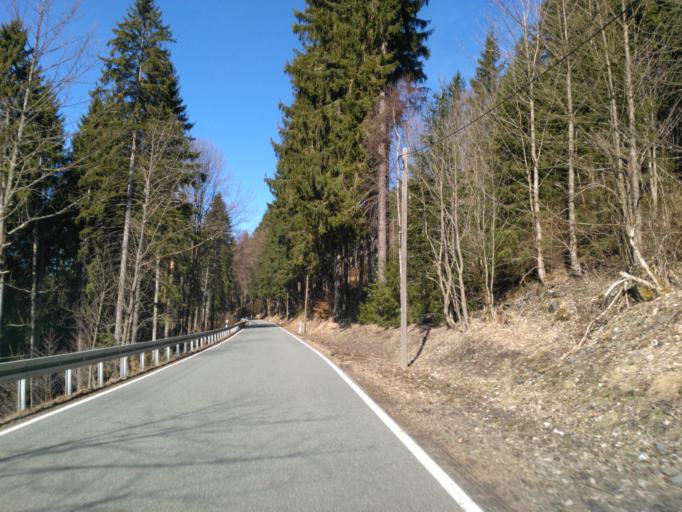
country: DE
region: Saxony
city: Pohla
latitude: 50.4515
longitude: 12.8682
